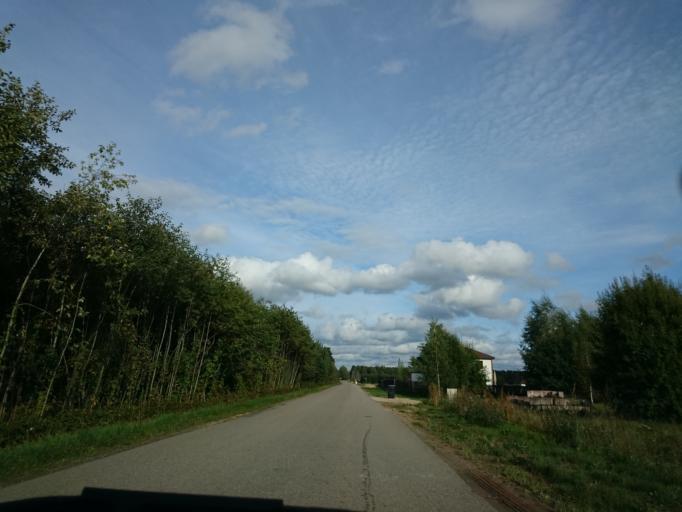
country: LV
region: Adazi
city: Adazi
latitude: 57.0642
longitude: 24.3536
